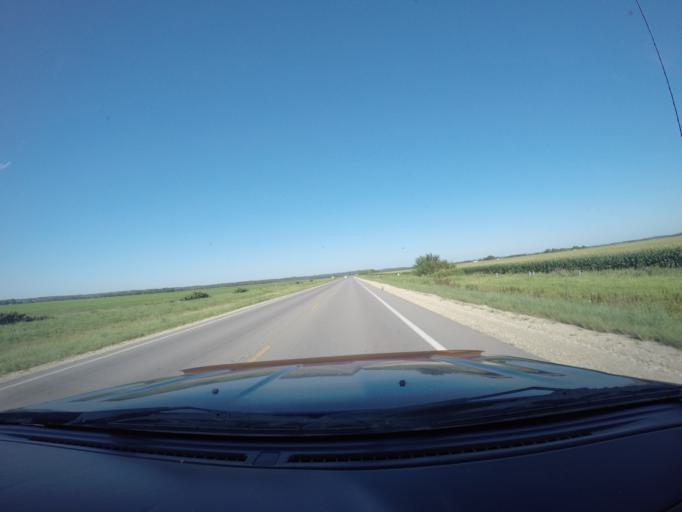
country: US
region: Kansas
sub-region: Jefferson County
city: Oskaloosa
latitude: 39.0872
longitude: -95.4366
